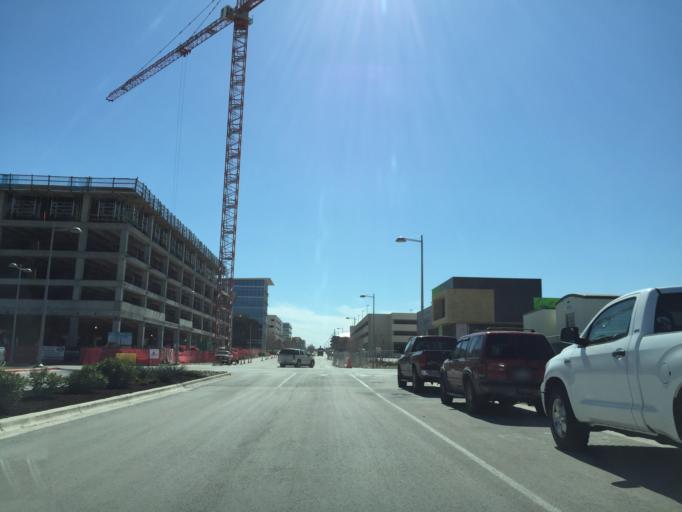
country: US
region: Texas
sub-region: Travis County
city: Wells Branch
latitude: 30.4032
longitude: -97.7190
